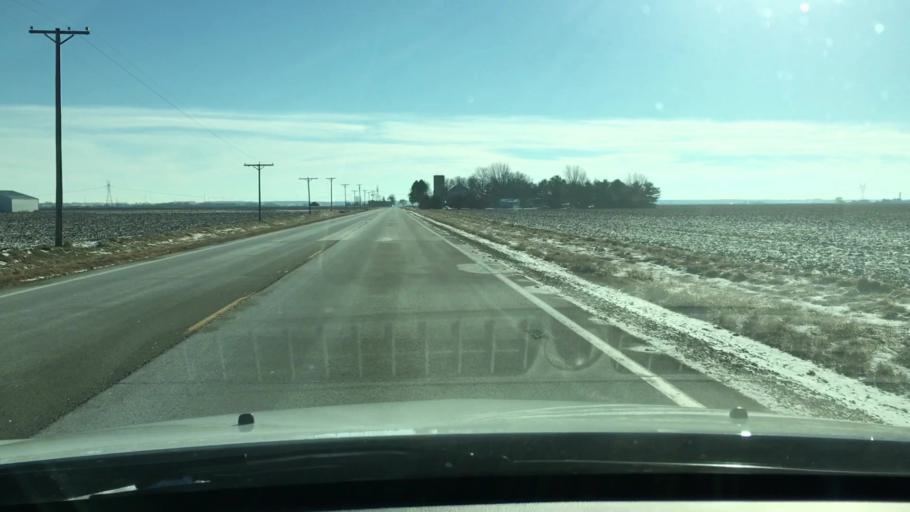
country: US
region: Illinois
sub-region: Ogle County
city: Rochelle
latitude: 41.8102
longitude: -89.0834
